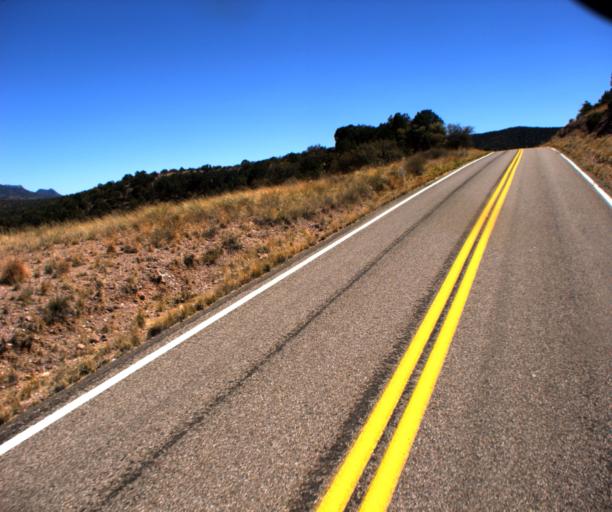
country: US
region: Arizona
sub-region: Cochise County
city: Sierra Vista
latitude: 31.4812
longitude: -110.4821
